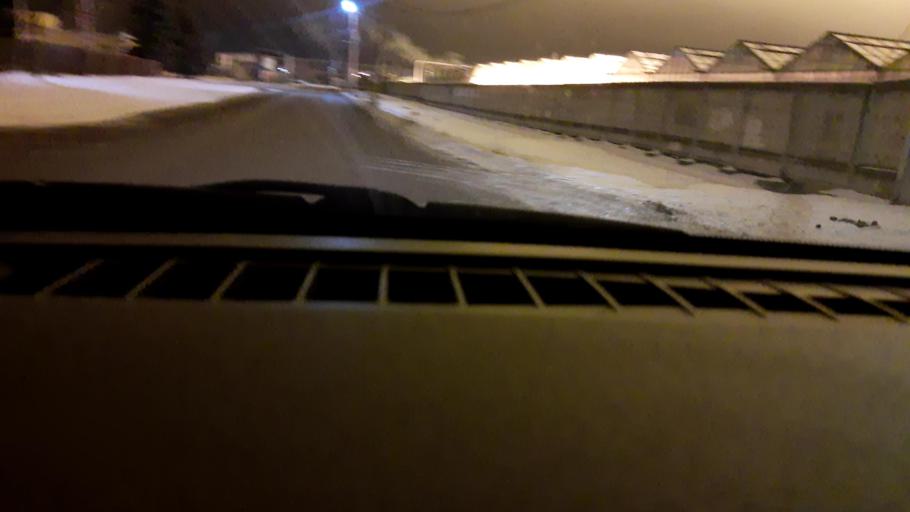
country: RU
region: Nizjnij Novgorod
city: Gorbatovka
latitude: 56.3090
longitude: 43.8139
